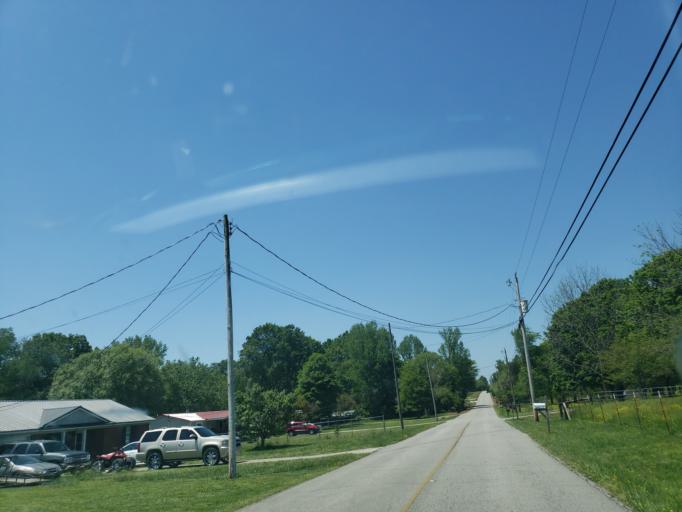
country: US
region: Alabama
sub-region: Madison County
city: Hazel Green
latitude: 34.9620
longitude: -86.6337
